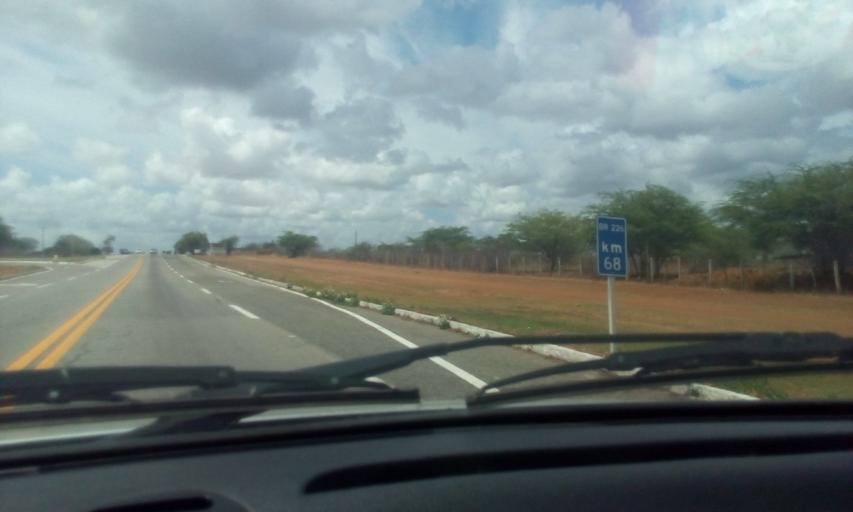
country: BR
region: Rio Grande do Norte
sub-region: Tangara
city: Tangara
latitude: -6.1023
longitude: -35.7036
